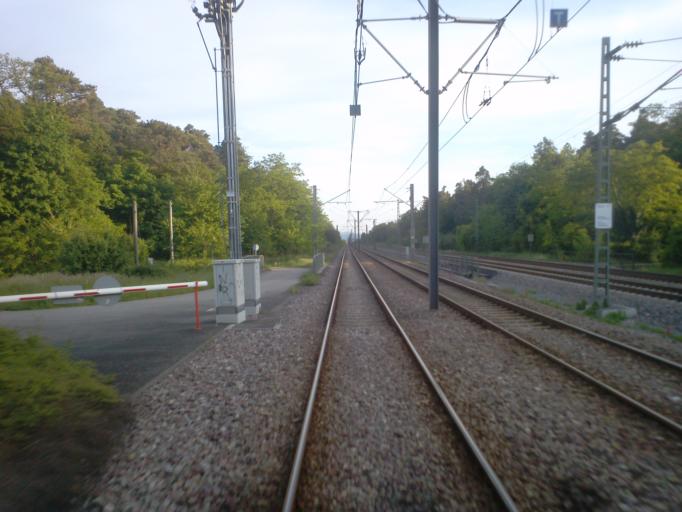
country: DE
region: Baden-Wuerttemberg
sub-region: Karlsruhe Region
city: Weingarten
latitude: 49.0963
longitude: 8.4731
